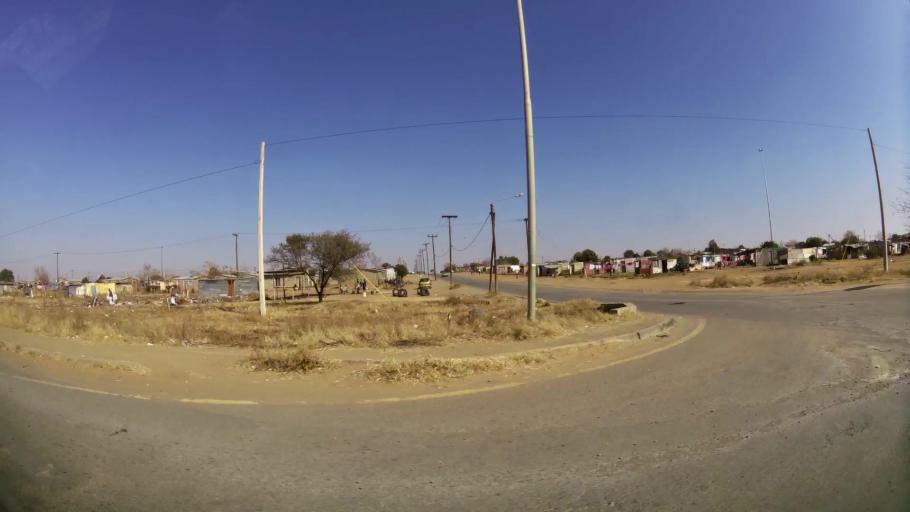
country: ZA
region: Orange Free State
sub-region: Mangaung Metropolitan Municipality
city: Bloemfontein
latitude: -29.1748
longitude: 26.2637
